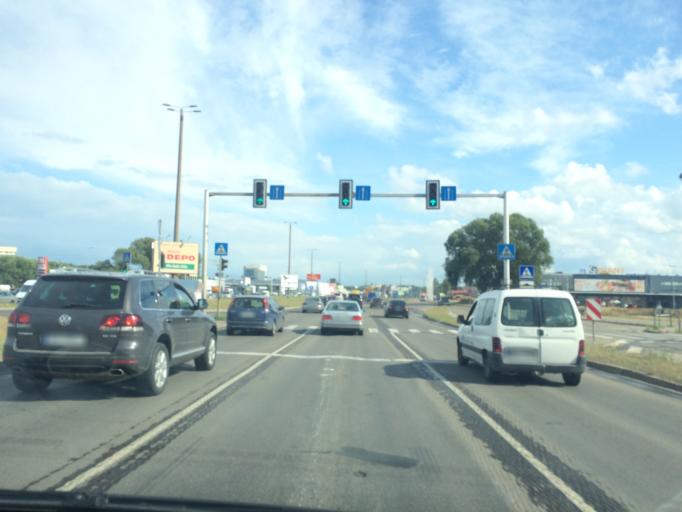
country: LV
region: Riga
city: Riga
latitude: 56.9332
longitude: 24.1440
